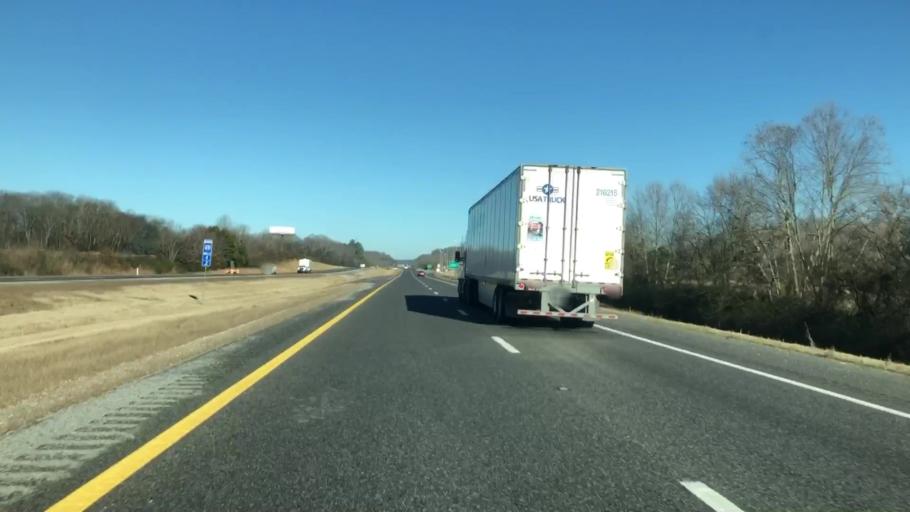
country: US
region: Alabama
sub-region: Limestone County
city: Ardmore
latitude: 35.0543
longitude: -86.8807
